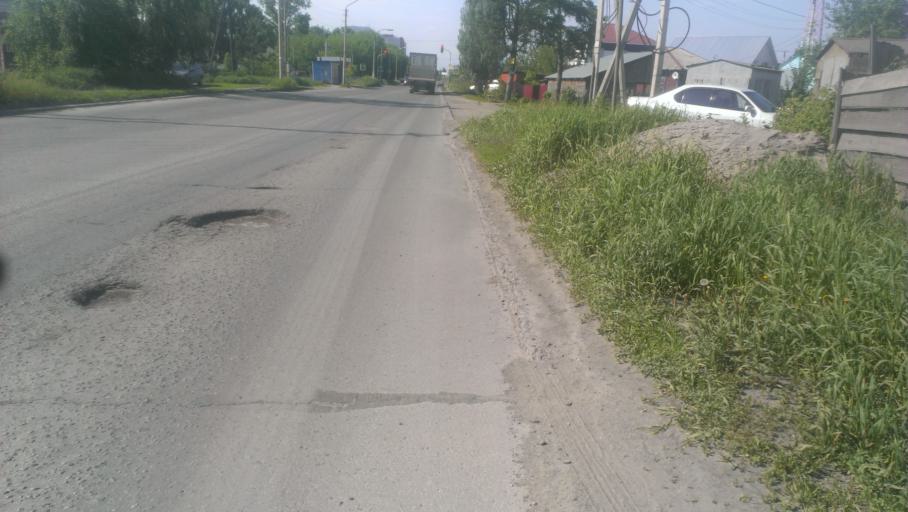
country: RU
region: Altai Krai
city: Novoaltaysk
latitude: 53.4062
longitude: 83.9446
